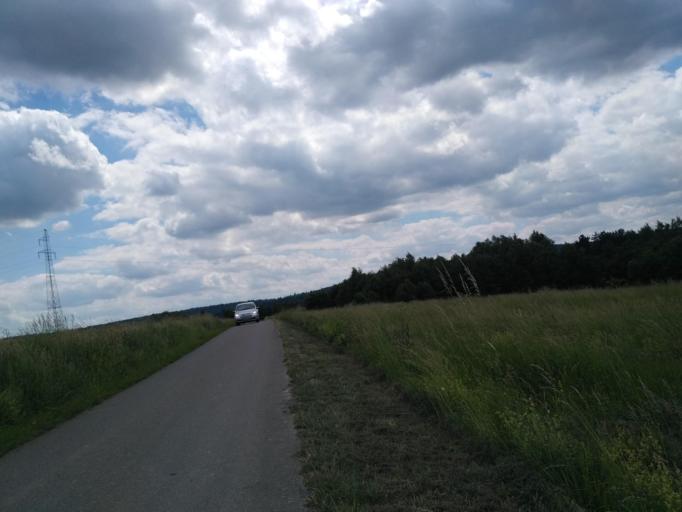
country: PL
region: Subcarpathian Voivodeship
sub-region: Powiat brzozowski
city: Nozdrzec
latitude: 49.7653
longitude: 22.1957
